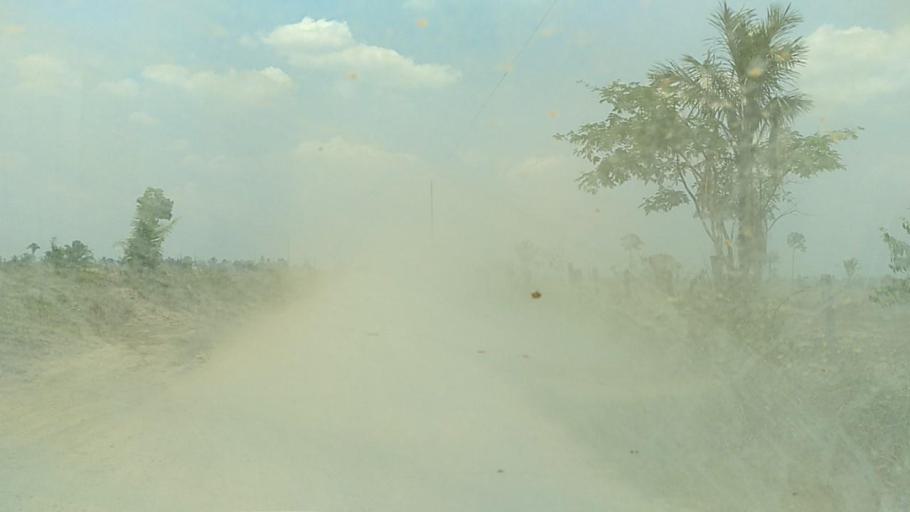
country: BR
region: Rondonia
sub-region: Porto Velho
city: Porto Velho
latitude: -8.7292
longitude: -63.2872
